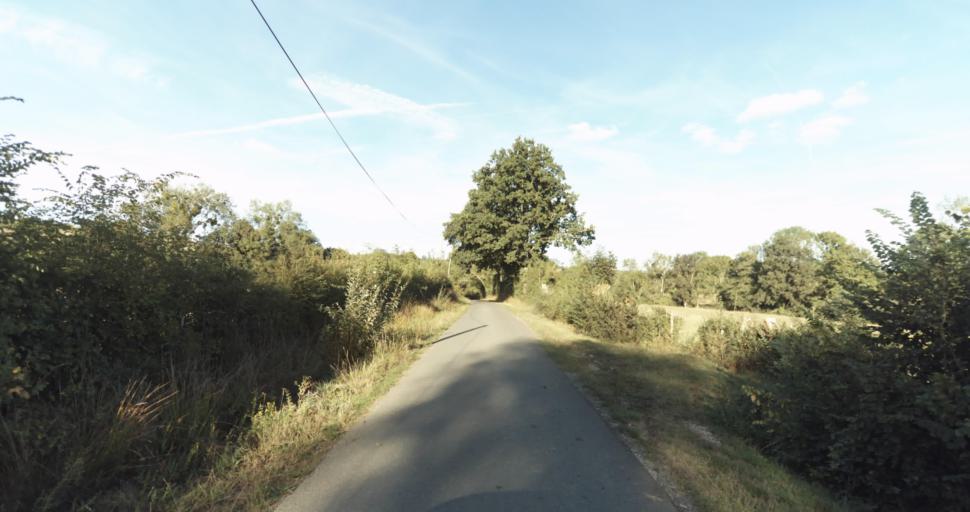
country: FR
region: Lower Normandy
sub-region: Departement de l'Orne
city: Vimoutiers
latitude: 48.8818
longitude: 0.1246
